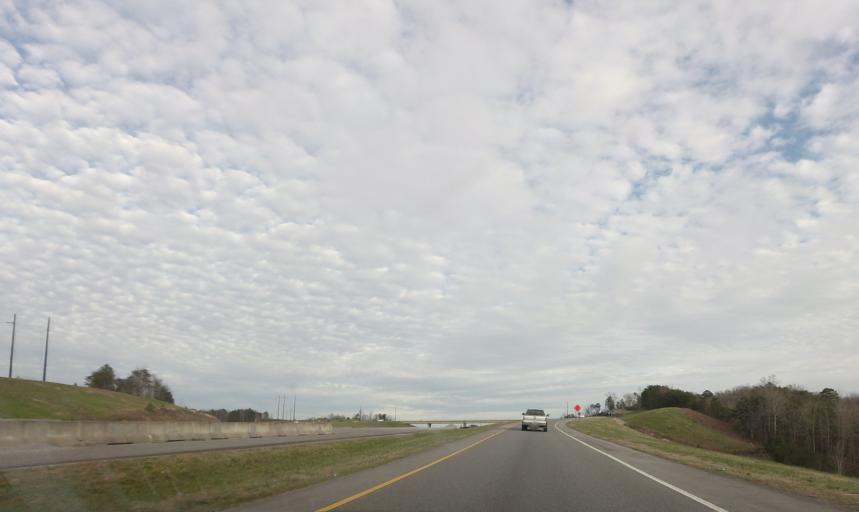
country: US
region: Alabama
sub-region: Jefferson County
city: Forestdale
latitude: 33.5889
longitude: -86.8608
